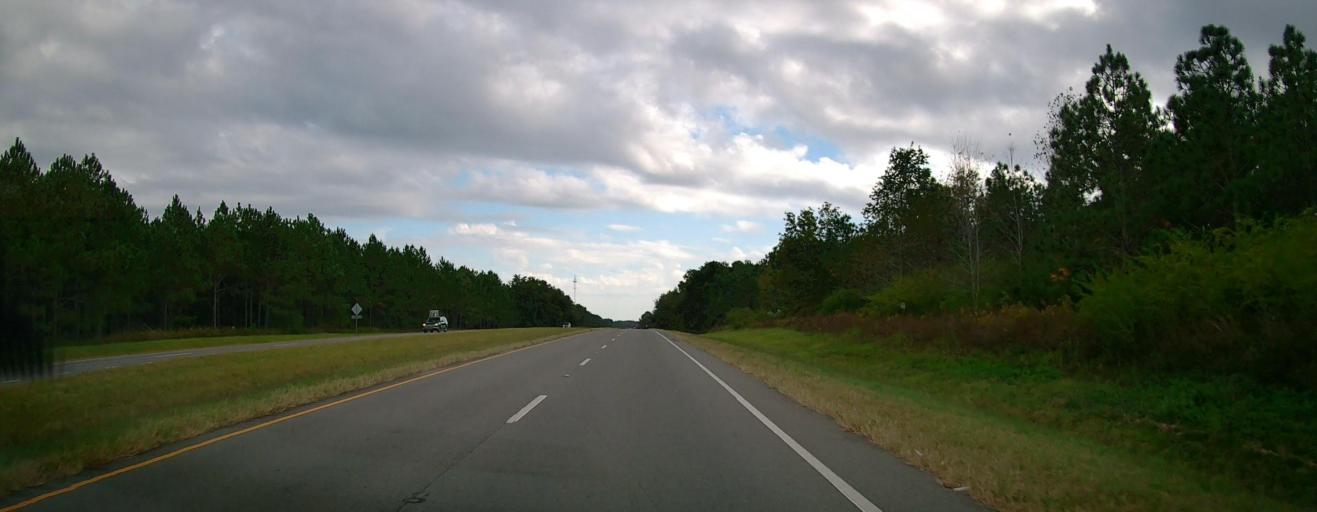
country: US
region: Georgia
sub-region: Thomas County
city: Meigs
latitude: 31.0749
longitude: -84.0793
